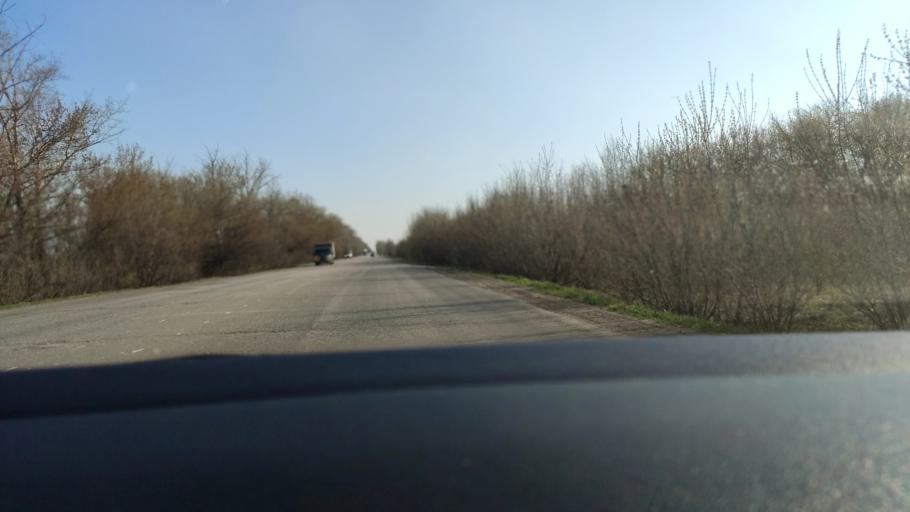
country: RU
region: Voronezj
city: Maslovka
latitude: 51.4918
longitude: 39.3080
